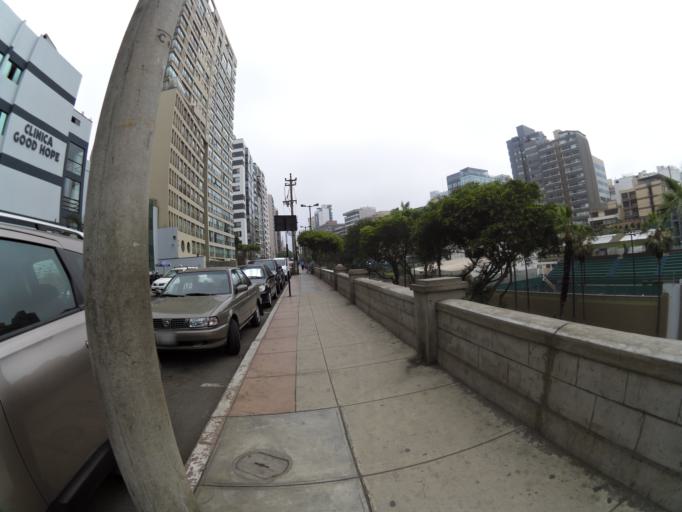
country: PE
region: Lima
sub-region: Lima
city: San Isidro
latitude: -12.1258
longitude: -77.0344
